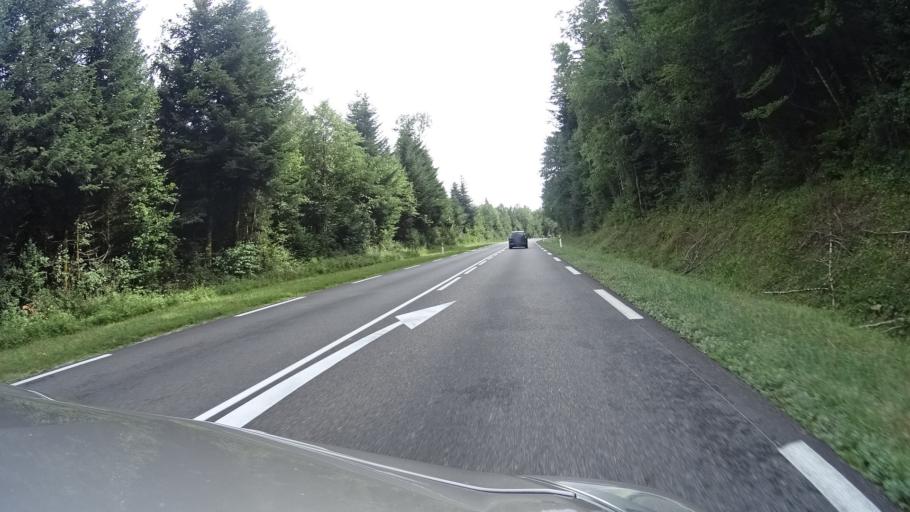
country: FR
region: Franche-Comte
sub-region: Departement du Jura
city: Champagnole
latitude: 46.7061
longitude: 5.9315
